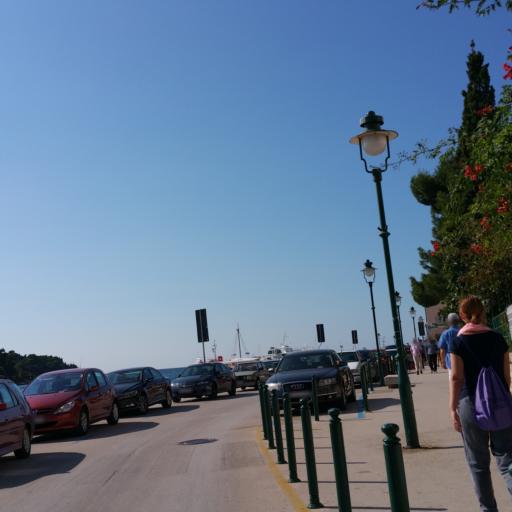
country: HR
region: Istarska
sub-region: Grad Rovinj
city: Rovinj
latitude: 45.0798
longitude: 13.6377
